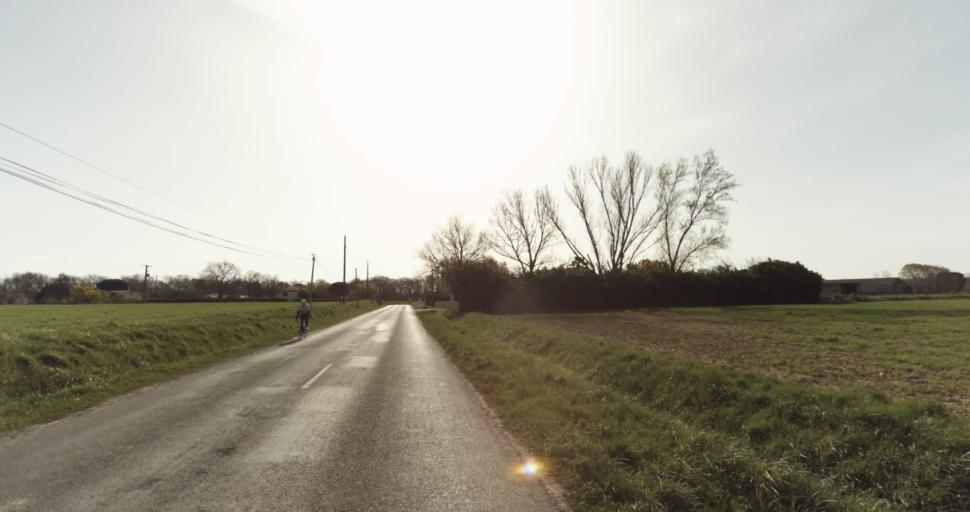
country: FR
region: Midi-Pyrenees
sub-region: Departement du Tarn
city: Saint-Sulpice-la-Pointe
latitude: 43.7700
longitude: 1.7039
